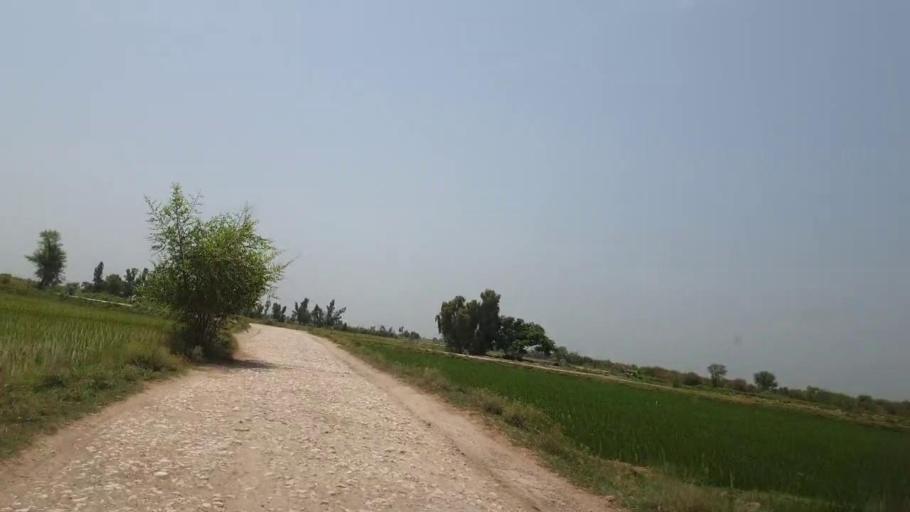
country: PK
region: Sindh
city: Shikarpur
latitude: 27.8839
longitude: 68.6285
